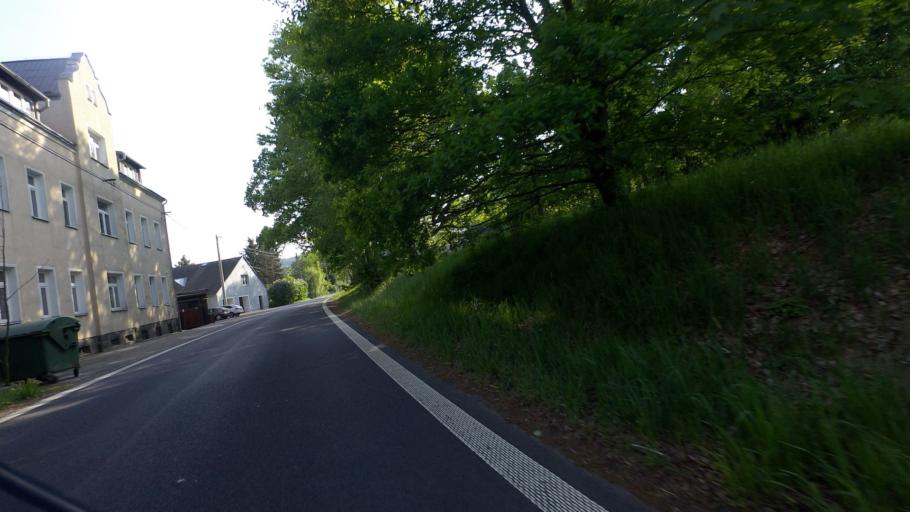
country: CZ
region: Ustecky
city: Dolni Poustevna
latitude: 51.0001
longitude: 14.2956
